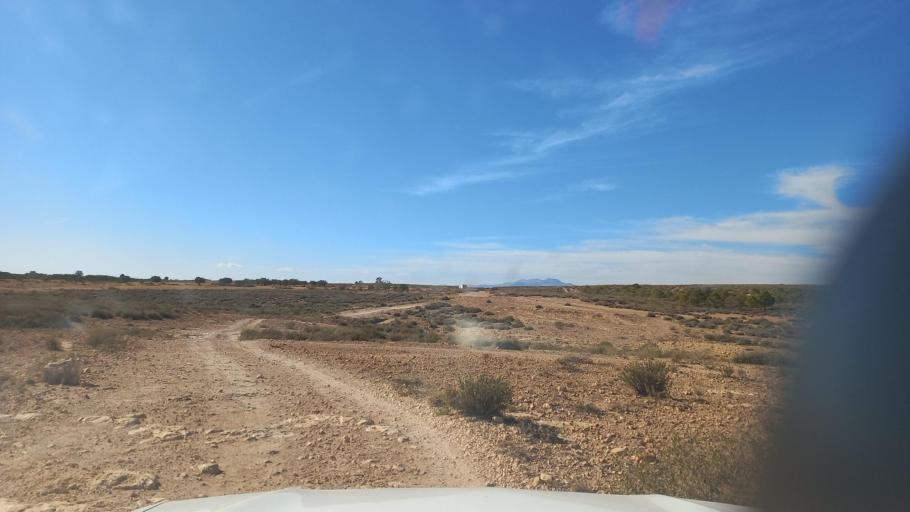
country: TN
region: Al Qasrayn
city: Kasserine
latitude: 35.2150
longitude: 8.9820
